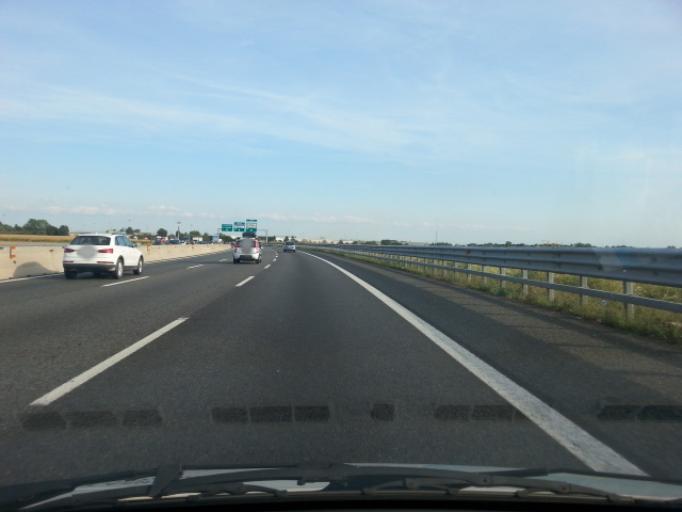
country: IT
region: Piedmont
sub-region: Provincia di Torino
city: Tetti Neirotti
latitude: 45.0441
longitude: 7.5501
